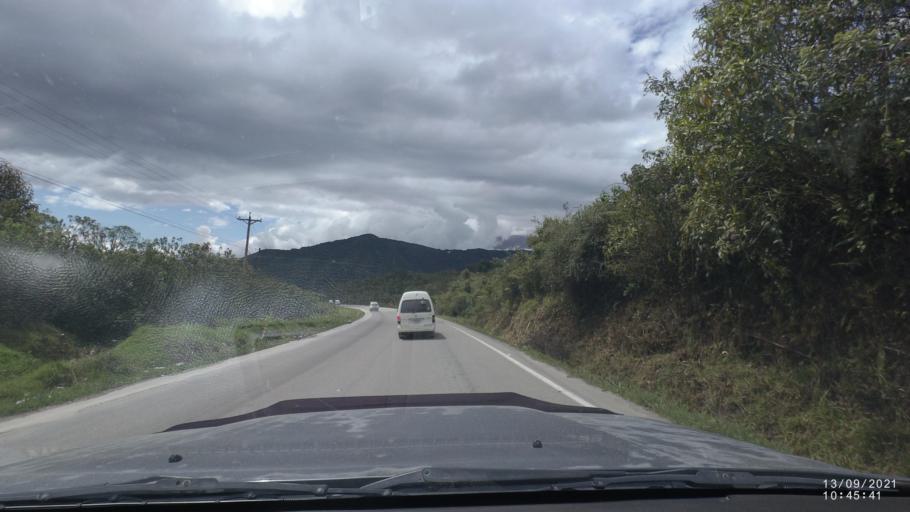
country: BO
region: Cochabamba
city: Colomi
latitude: -17.2035
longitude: -65.8738
